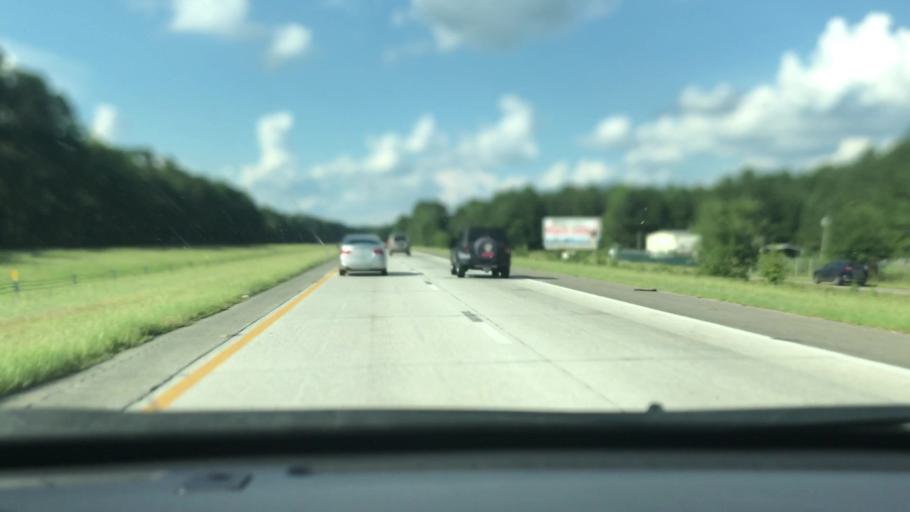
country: US
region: South Carolina
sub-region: Florence County
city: Timmonsville
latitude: 34.0850
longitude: -79.9368
